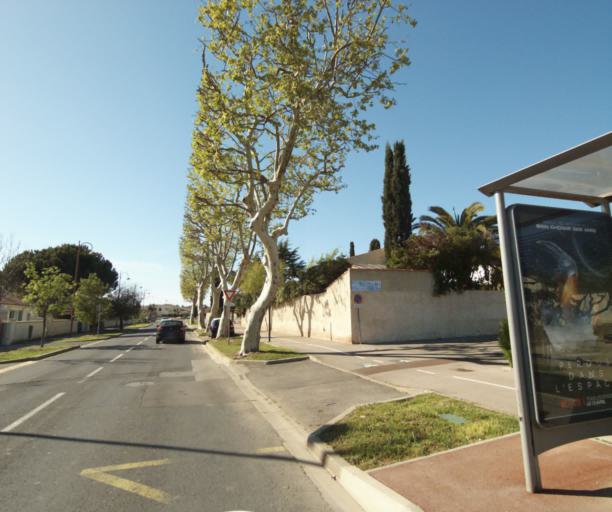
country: FR
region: Languedoc-Roussillon
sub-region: Departement de l'Herault
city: Perols
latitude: 43.5690
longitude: 3.9453
